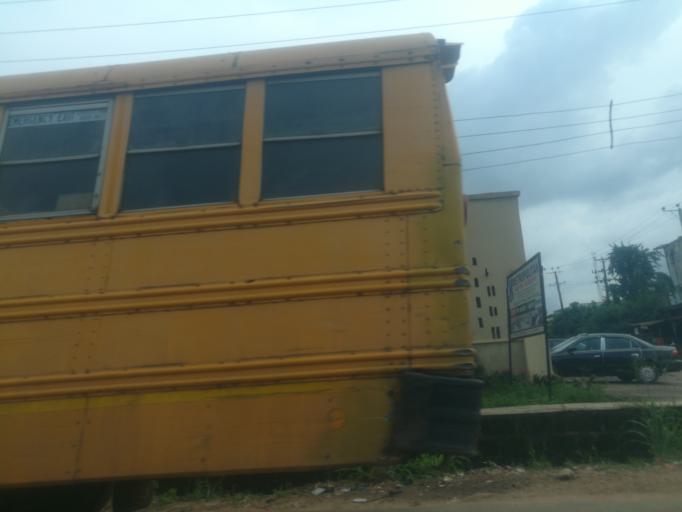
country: NG
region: Oyo
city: Ibadan
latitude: 7.3681
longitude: 3.8559
